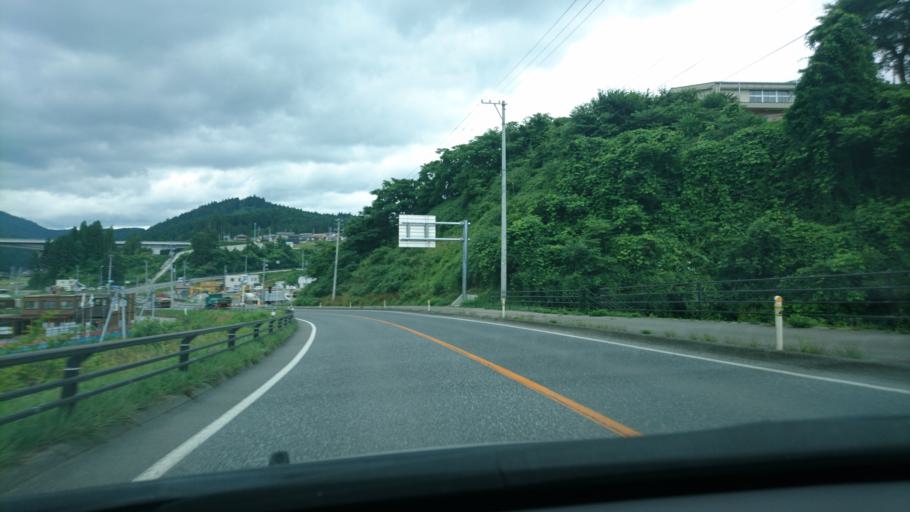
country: JP
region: Iwate
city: Ofunato
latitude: 38.9886
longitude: 141.6157
